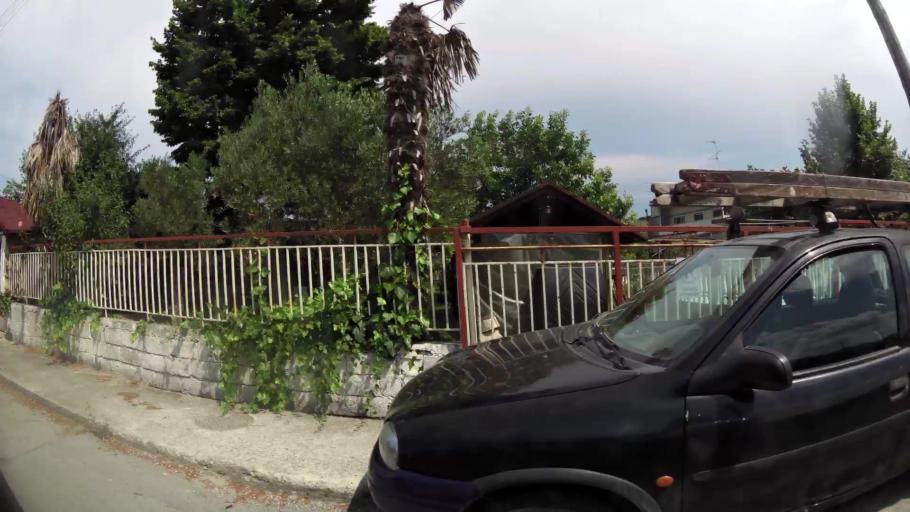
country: GR
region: Central Macedonia
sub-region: Nomos Pierias
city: Korinos
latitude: 40.3197
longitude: 22.5810
